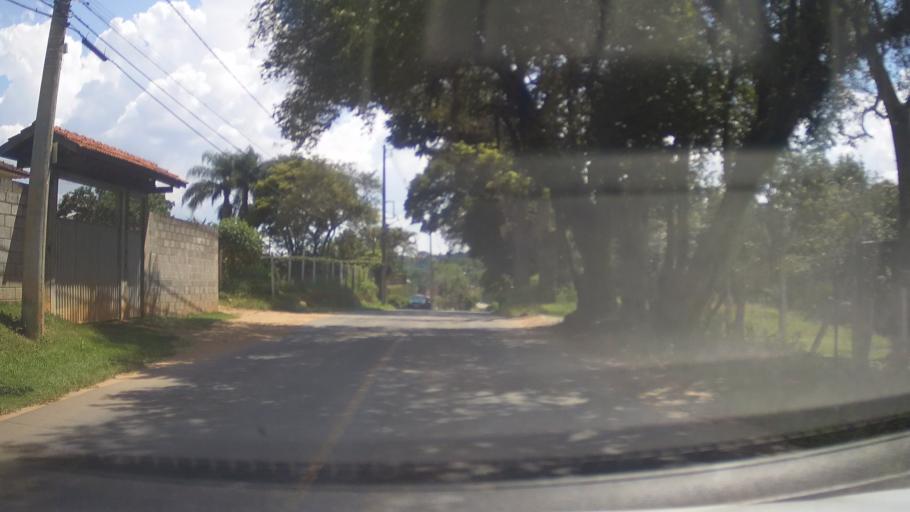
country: BR
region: Sao Paulo
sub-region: Campo Limpo Paulista
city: Campo Limpo Paulista
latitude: -23.1347
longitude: -46.8136
